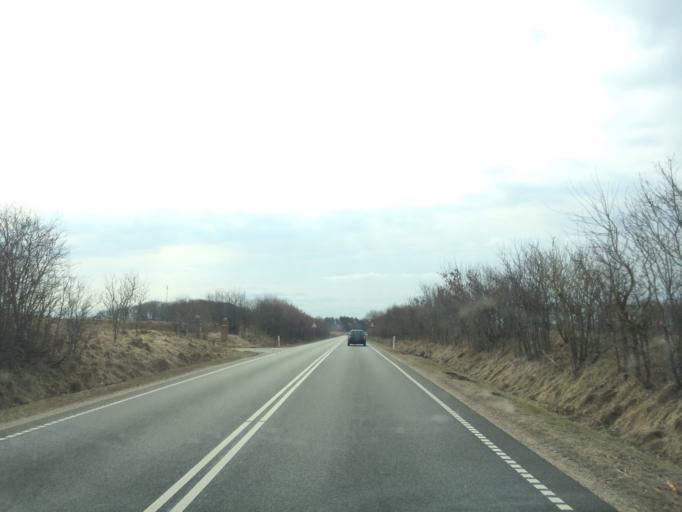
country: DK
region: Central Jutland
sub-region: Ringkobing-Skjern Kommune
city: Skjern
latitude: 55.9954
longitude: 8.5061
